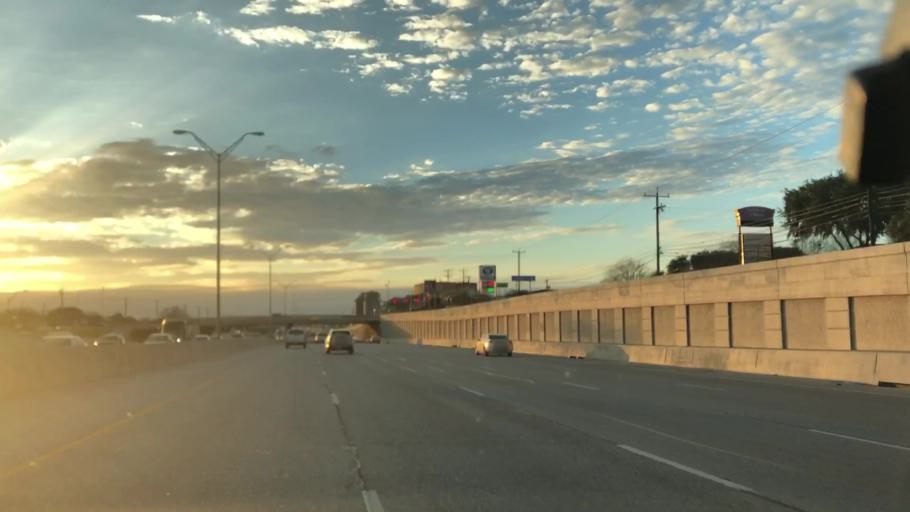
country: US
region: Texas
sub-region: Bexar County
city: Windcrest
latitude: 29.5166
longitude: -98.4205
